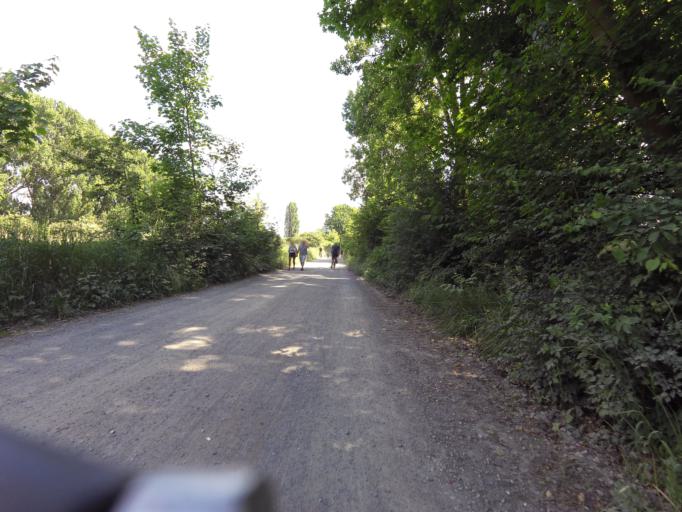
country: DE
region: Rheinland-Pfalz
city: Nackenheim
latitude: 49.9248
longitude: 8.3531
